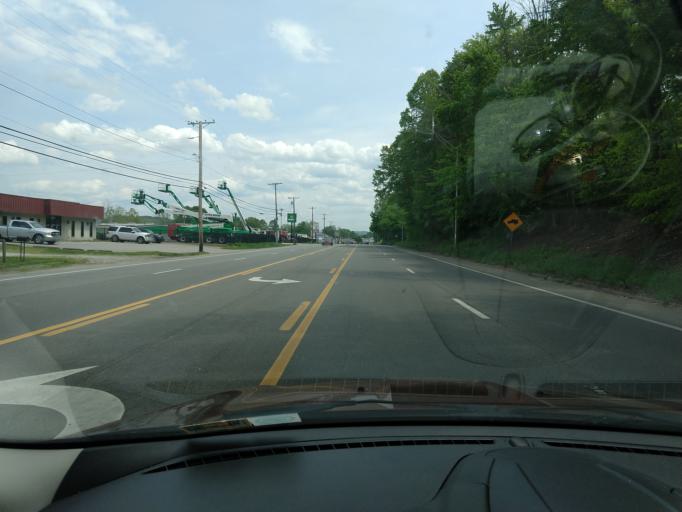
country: US
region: West Virginia
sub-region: Kanawha County
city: Dunbar
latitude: 38.3741
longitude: -81.7765
